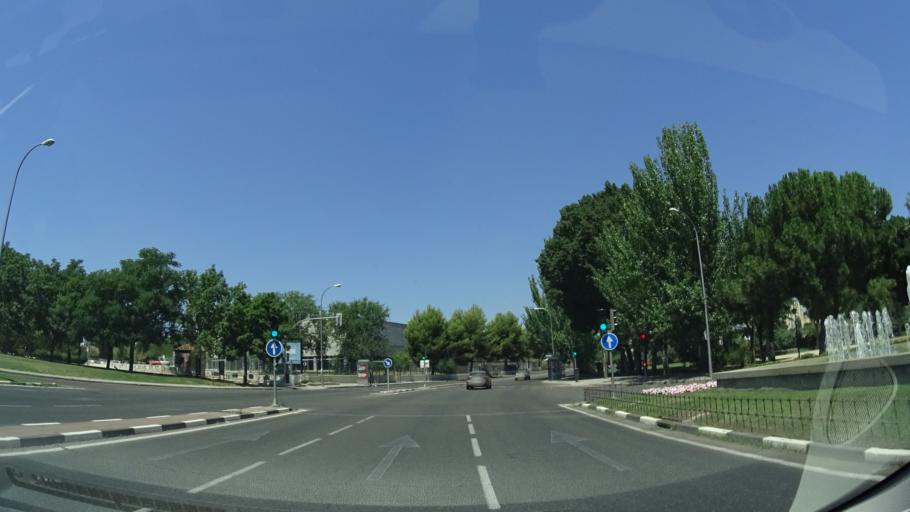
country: ES
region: Madrid
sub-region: Provincia de Madrid
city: Latina
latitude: 40.3780
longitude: -3.7553
